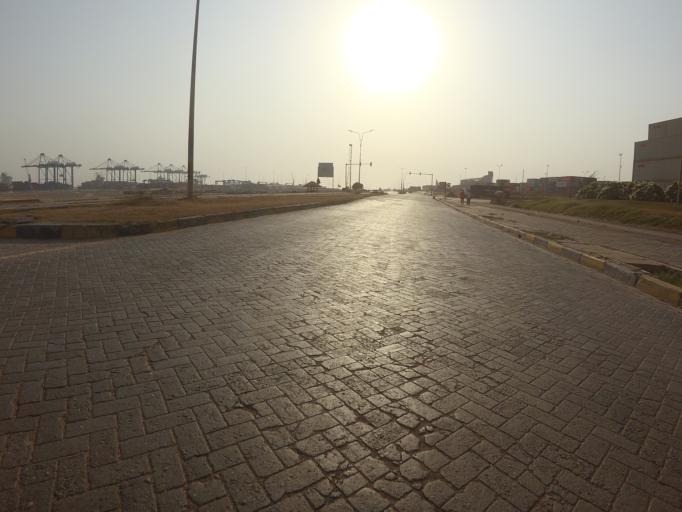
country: GH
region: Greater Accra
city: Tema
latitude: 5.6241
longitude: -0.0069
